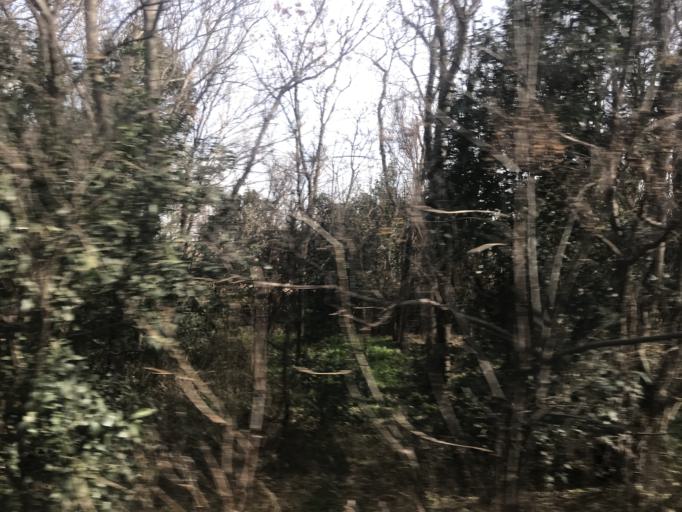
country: AR
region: Cordoba
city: Laguna Larga
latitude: -31.8076
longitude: -63.7762
